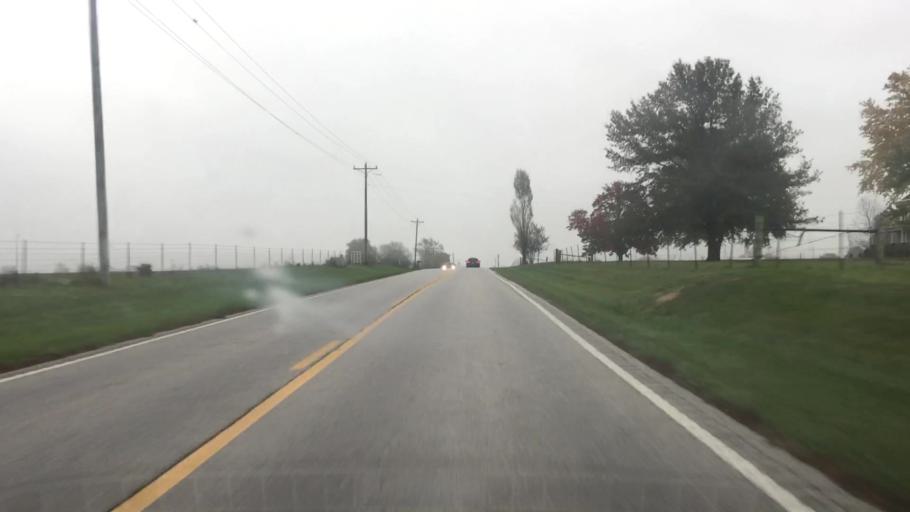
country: US
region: Missouri
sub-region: Callaway County
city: Fulton
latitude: 38.8739
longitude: -92.0613
